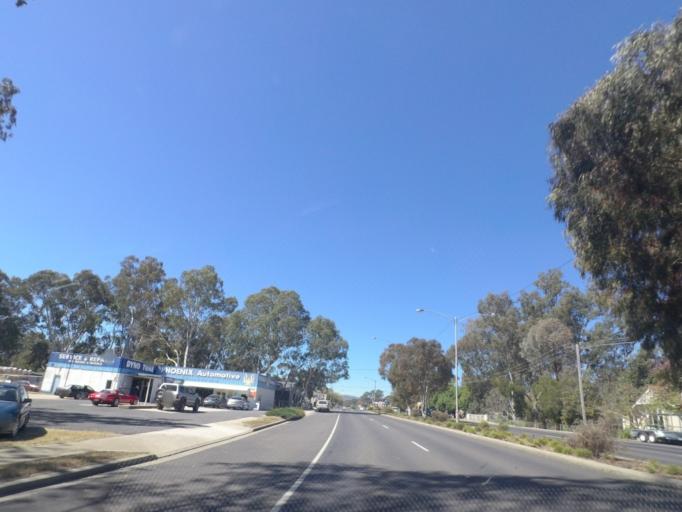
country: AU
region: Victoria
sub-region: Murrindindi
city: Kinglake West
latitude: -37.0215
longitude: 145.1245
